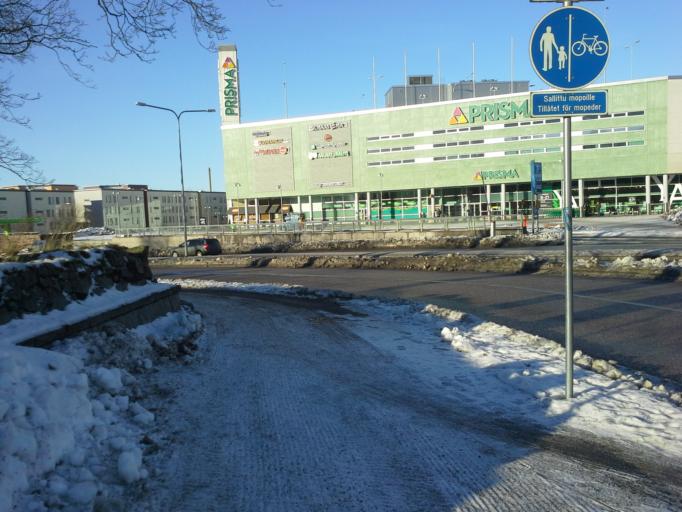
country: FI
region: Uusimaa
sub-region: Helsinki
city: Vantaa
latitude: 60.2272
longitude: 25.0111
